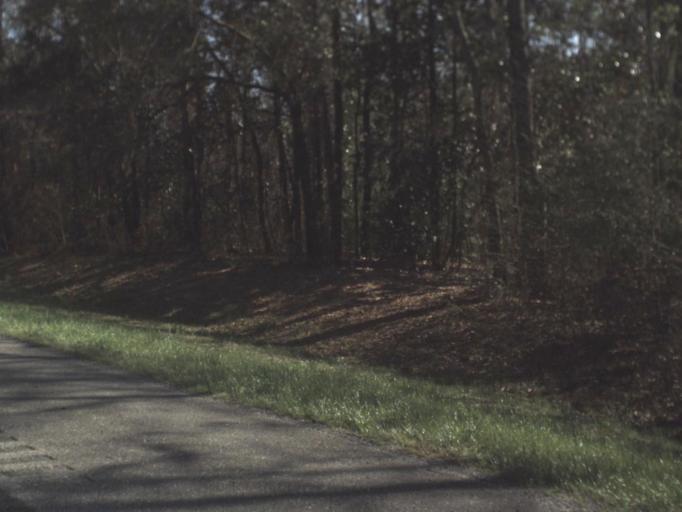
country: US
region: Florida
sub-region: Gadsden County
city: Gretna
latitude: 30.5837
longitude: -84.7125
